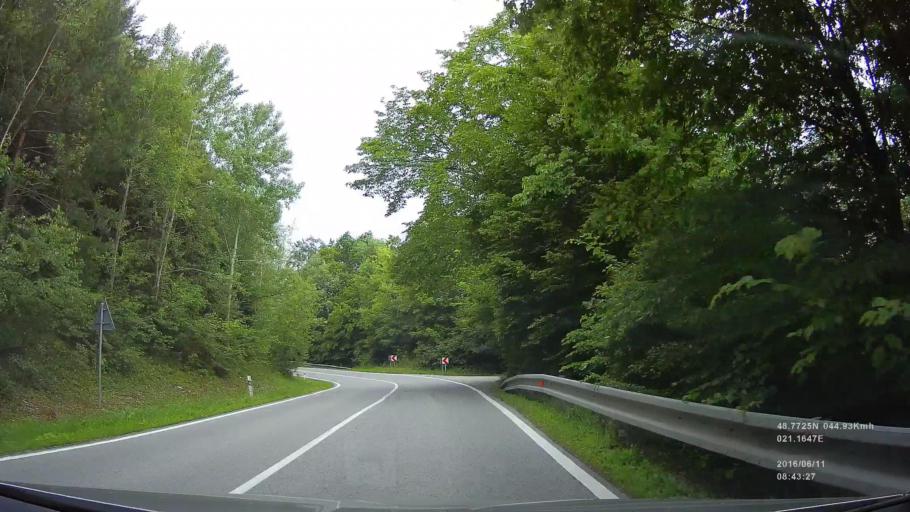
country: SK
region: Kosicky
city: Kosice
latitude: 48.7532
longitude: 21.2123
